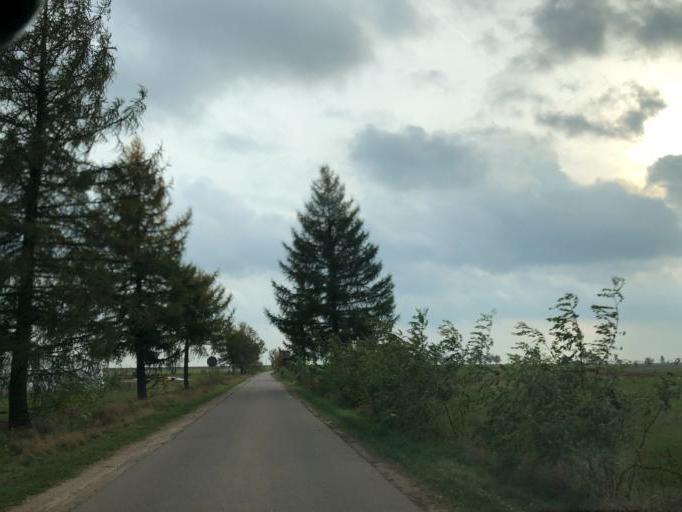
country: PL
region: Podlasie
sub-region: Lomza
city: Lomza
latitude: 53.1358
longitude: 21.9738
